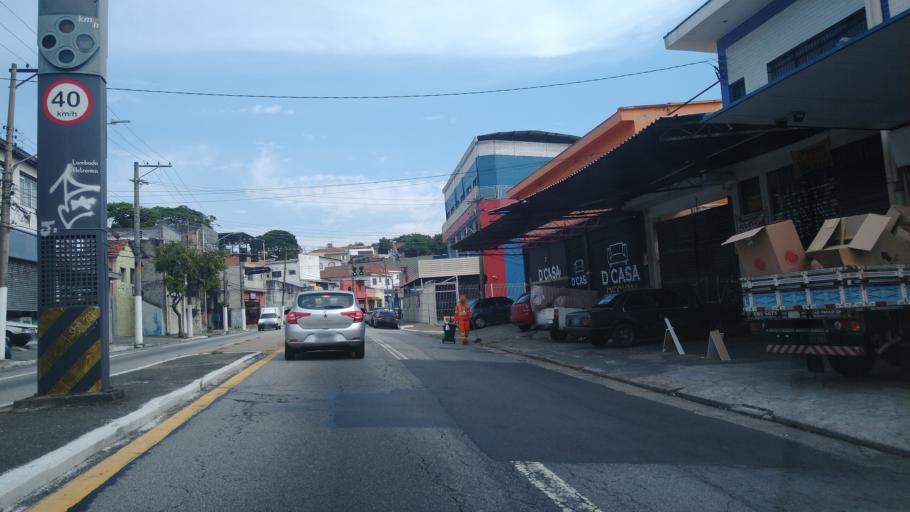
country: BR
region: Sao Paulo
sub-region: Sao Paulo
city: Sao Paulo
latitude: -23.4794
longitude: -46.6621
